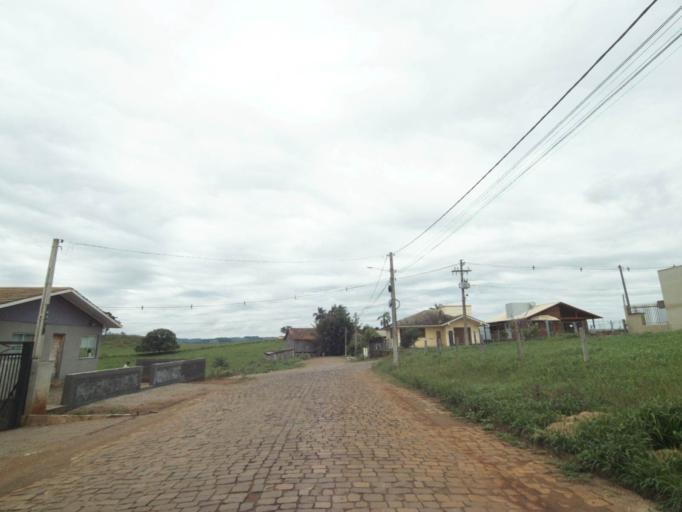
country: BR
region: Rio Grande do Sul
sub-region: Lagoa Vermelha
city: Lagoa Vermelha
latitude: -28.2178
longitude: -51.5329
